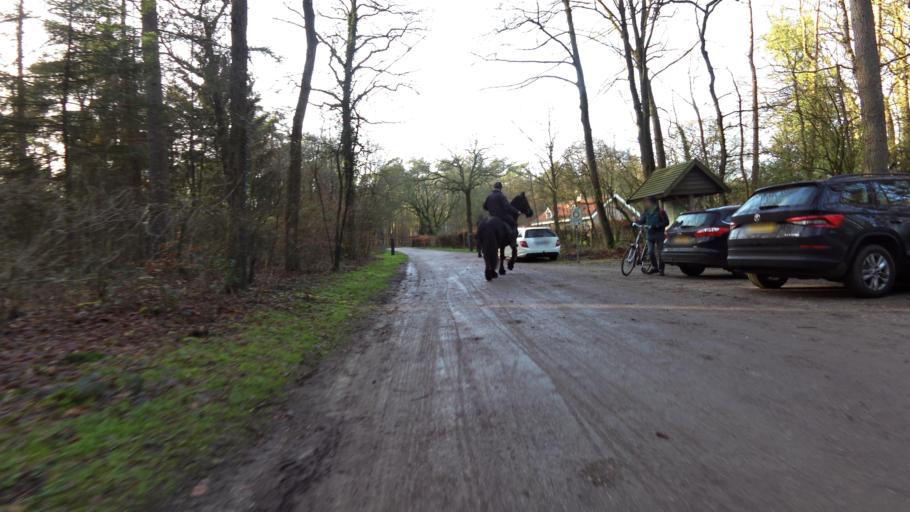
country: NL
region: Gelderland
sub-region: Gemeente Epe
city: Vaassen
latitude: 52.2522
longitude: 5.9210
